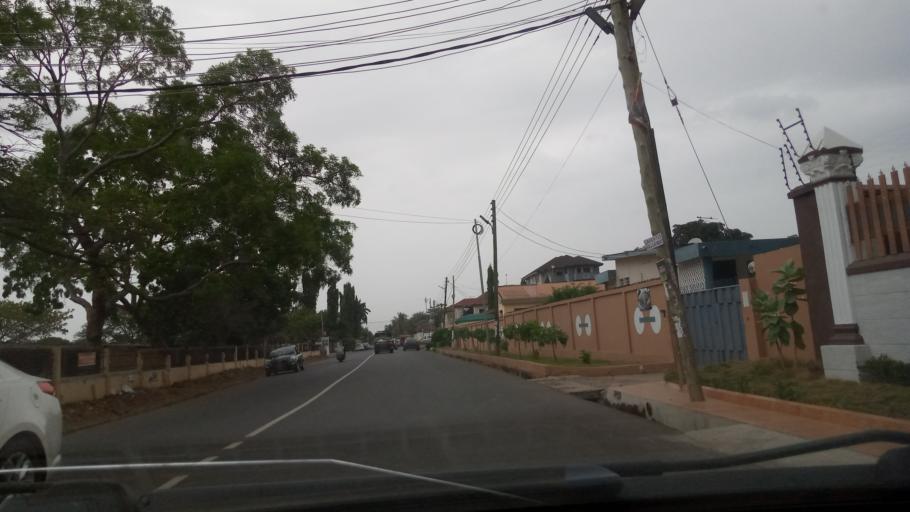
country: GH
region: Greater Accra
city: Dome
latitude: 5.6149
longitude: -0.2036
